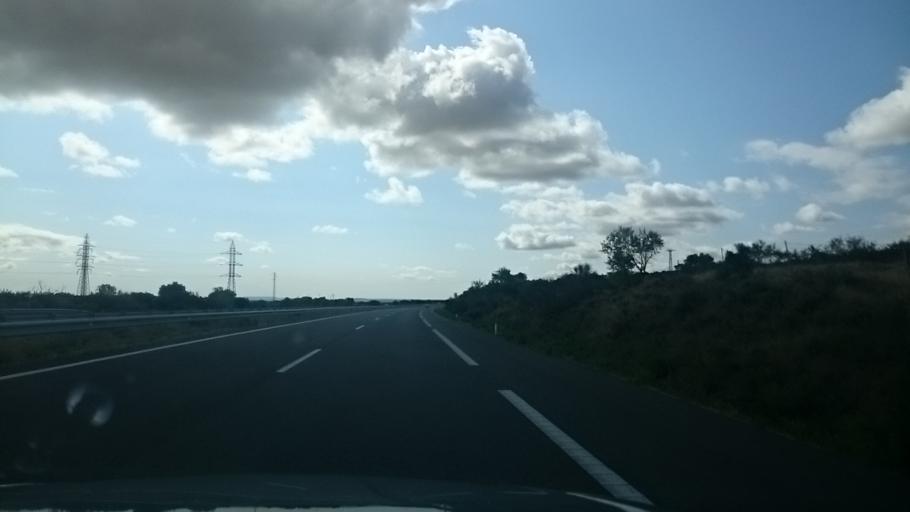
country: ES
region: La Rioja
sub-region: Provincia de La Rioja
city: Calahorra
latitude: 42.2828
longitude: -1.9437
